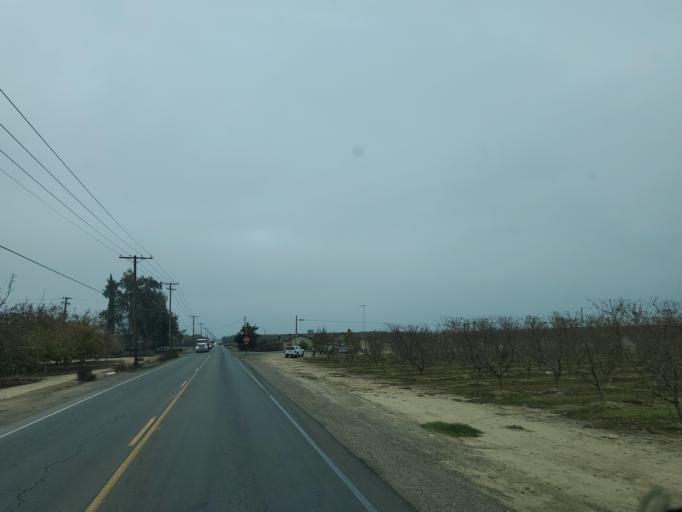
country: US
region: California
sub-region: Stanislaus County
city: Hughson
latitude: 37.5512
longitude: -120.8665
